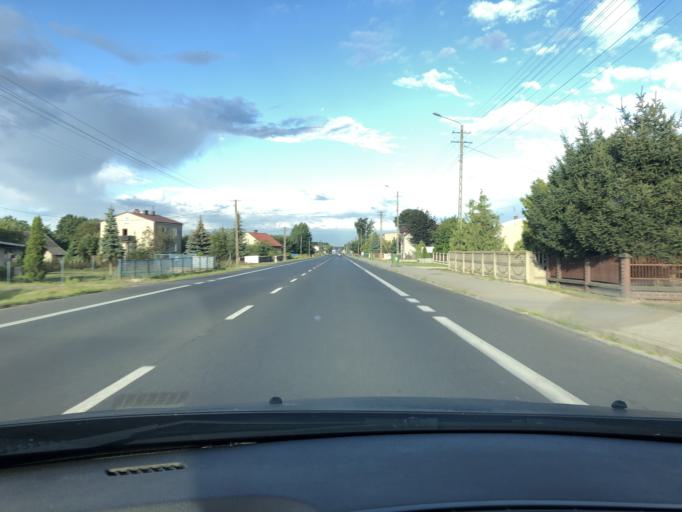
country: PL
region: Lodz Voivodeship
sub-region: Powiat wieruszowski
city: Wieruszow
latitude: 51.2986
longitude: 18.2078
